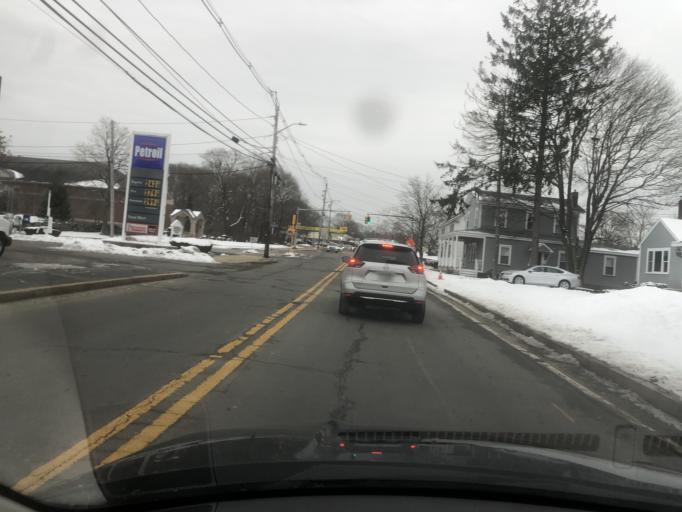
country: US
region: Massachusetts
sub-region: Middlesex County
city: Tewksbury
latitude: 42.6070
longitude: -71.2269
